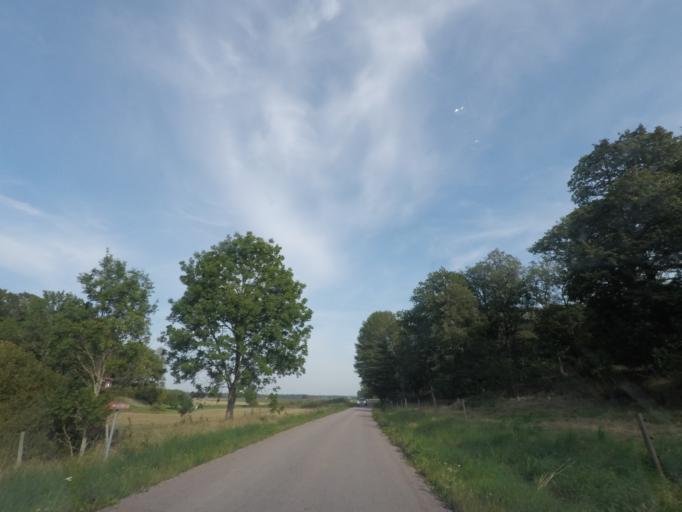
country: SE
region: Vaestmanland
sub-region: Kungsors Kommun
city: Kungsoer
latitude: 59.4836
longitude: 16.1792
